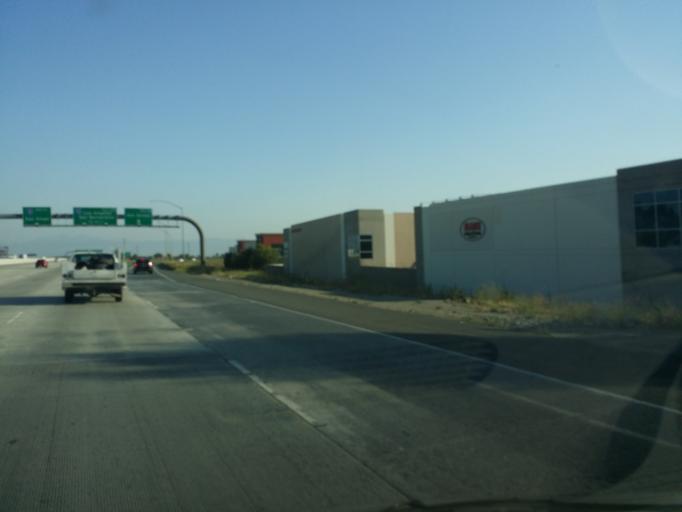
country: US
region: California
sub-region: San Bernardino County
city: Rancho Cucamonga
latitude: 34.0828
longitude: -117.5450
